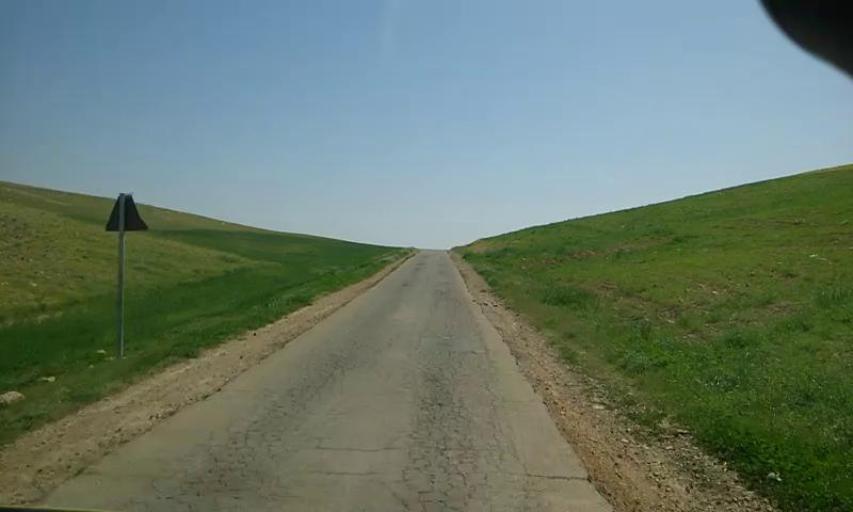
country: PS
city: `Arab ar Rashaydah
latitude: 31.5509
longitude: 35.2523
